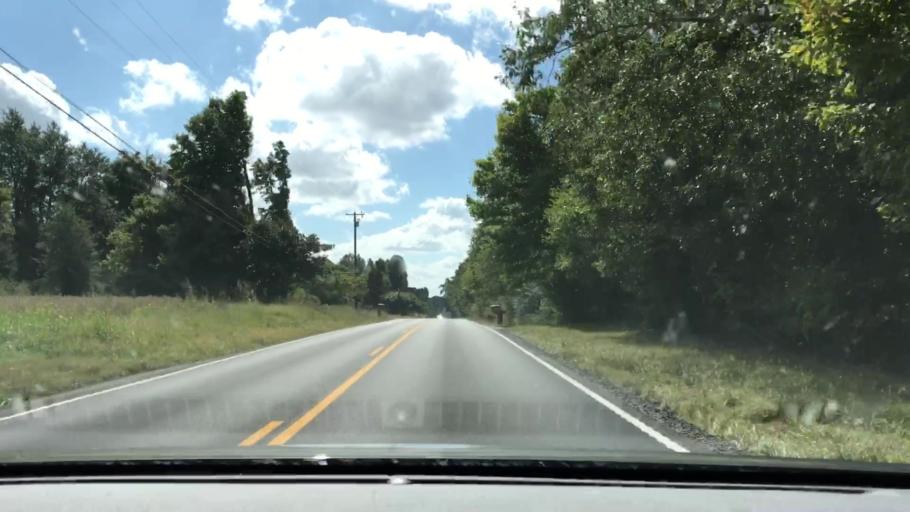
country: US
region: Kentucky
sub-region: Graves County
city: Mayfield
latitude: 36.7958
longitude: -88.5955
